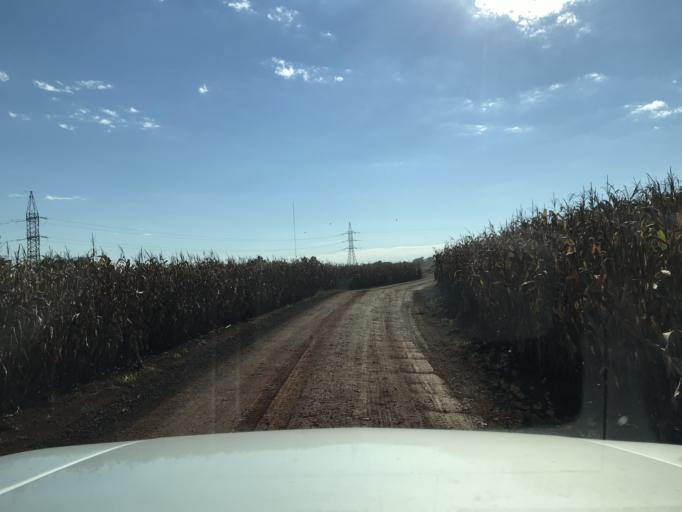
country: BR
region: Parana
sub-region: Palotina
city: Palotina
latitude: -24.2743
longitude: -53.8187
